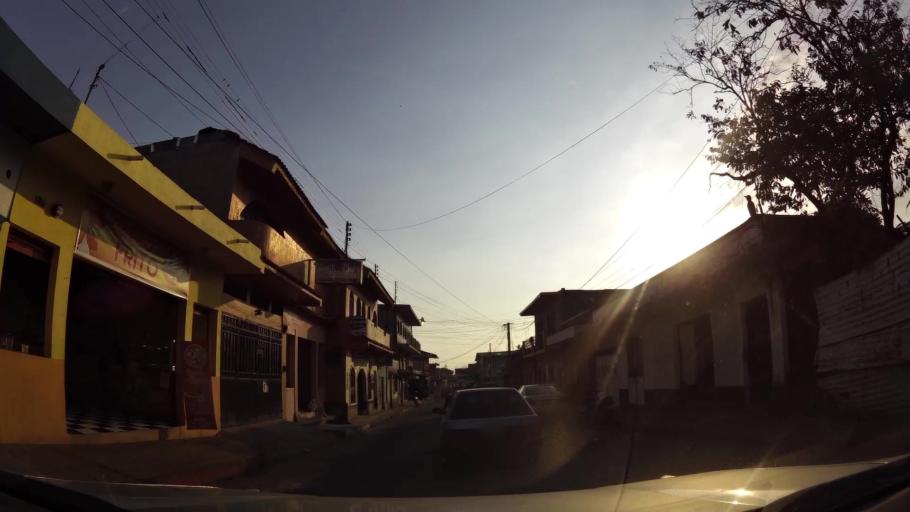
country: GT
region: Retalhuleu
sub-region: Municipio de Retalhuleu
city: Retalhuleu
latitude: 14.5398
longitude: -91.6752
